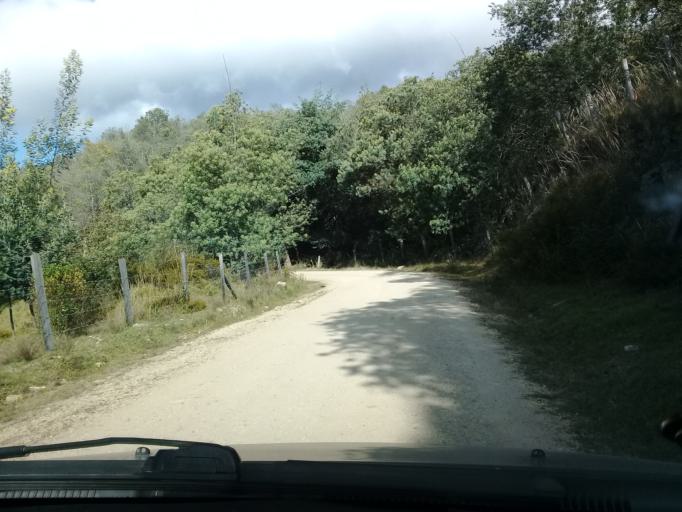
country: CO
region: Cundinamarca
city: Guatavita
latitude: 4.9421
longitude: -73.8657
